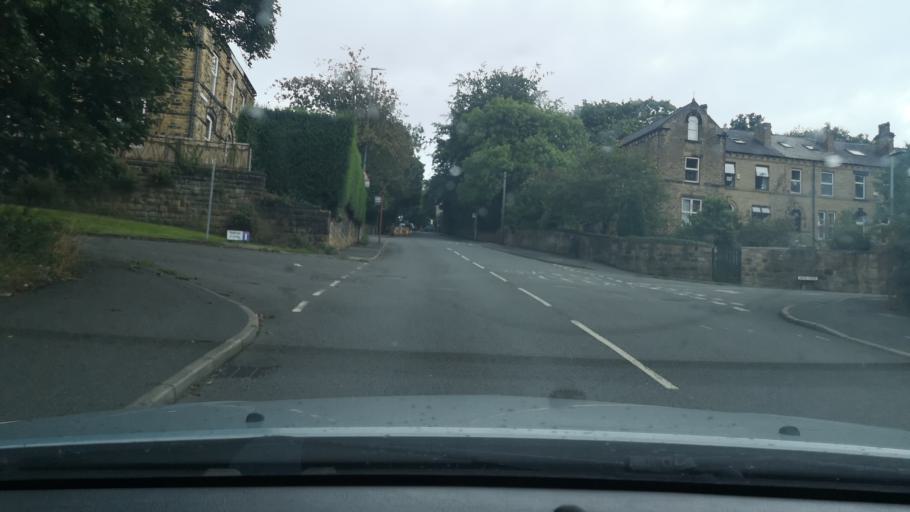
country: GB
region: England
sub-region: Kirklees
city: Batley
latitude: 53.7179
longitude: -1.6336
